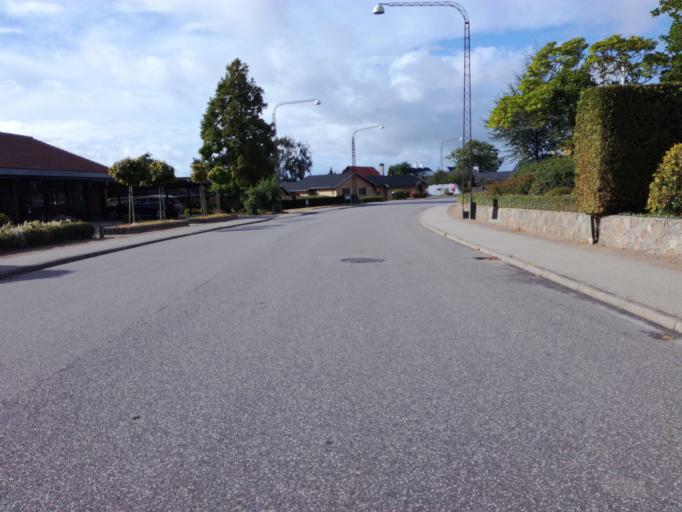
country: DK
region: South Denmark
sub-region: Fredericia Kommune
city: Fredericia
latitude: 55.5788
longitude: 9.7800
